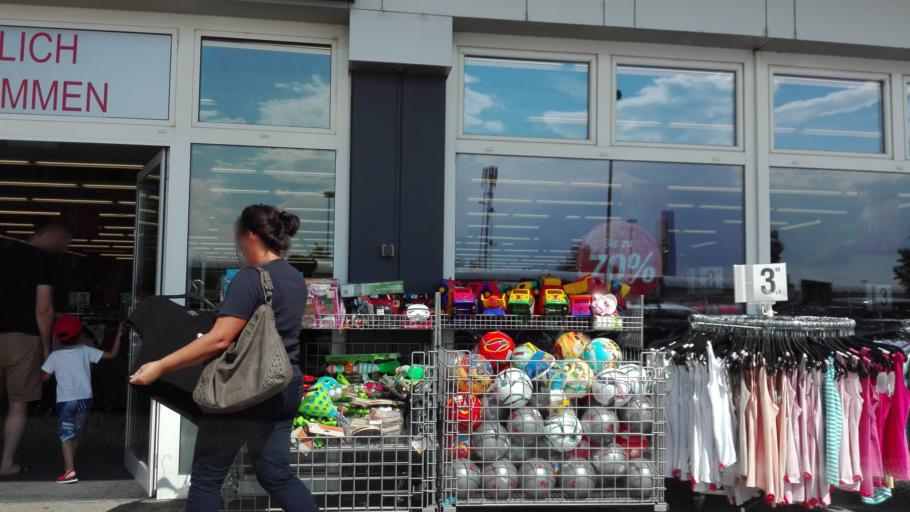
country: AT
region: Upper Austria
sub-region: Politischer Bezirk Perg
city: Perg
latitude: 48.2392
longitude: 14.6276
